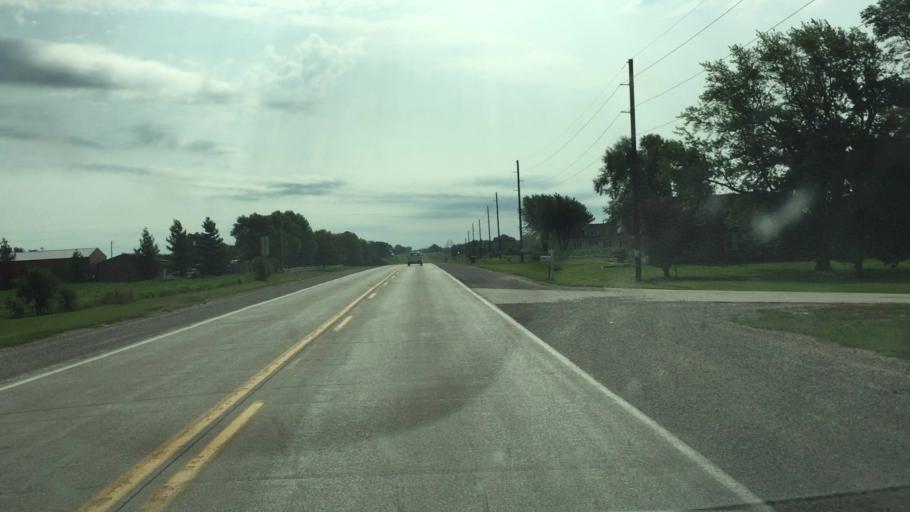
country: US
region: Illinois
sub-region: Hancock County
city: Nauvoo
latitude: 40.6390
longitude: -91.5519
